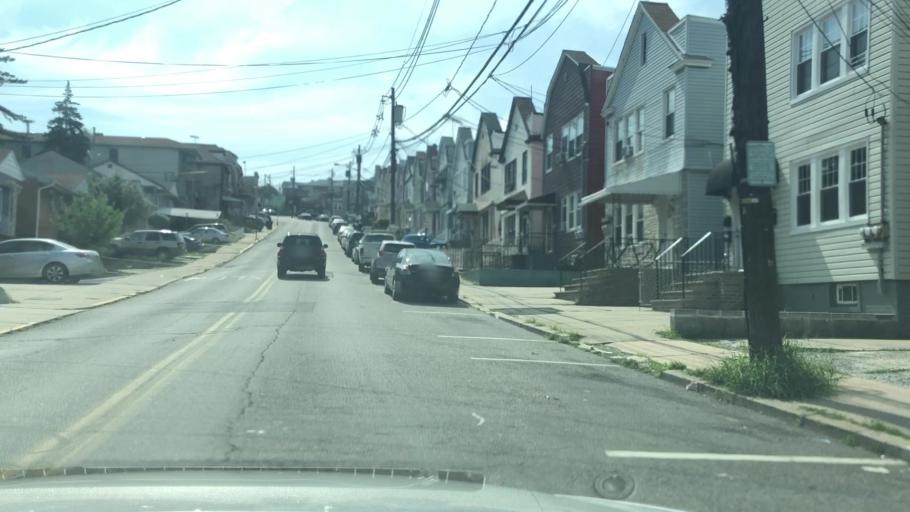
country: US
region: New Jersey
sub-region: Hudson County
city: North Bergen
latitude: 40.8041
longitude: -74.0175
